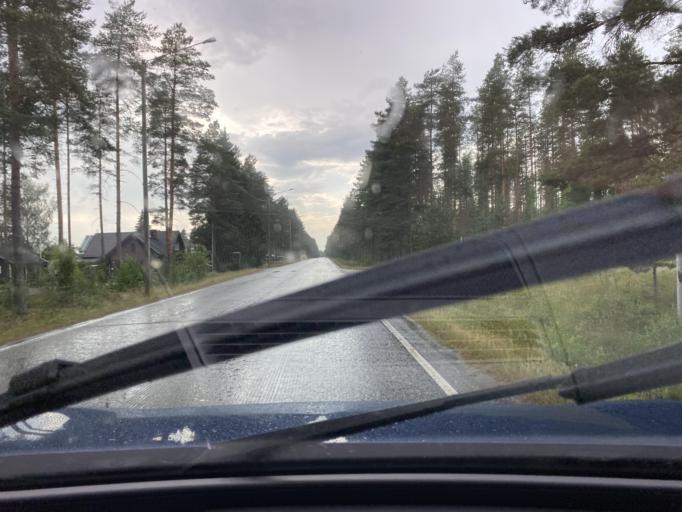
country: FI
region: Central Ostrobothnia
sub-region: Kaustinen
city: Veteli
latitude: 63.4690
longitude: 23.8229
